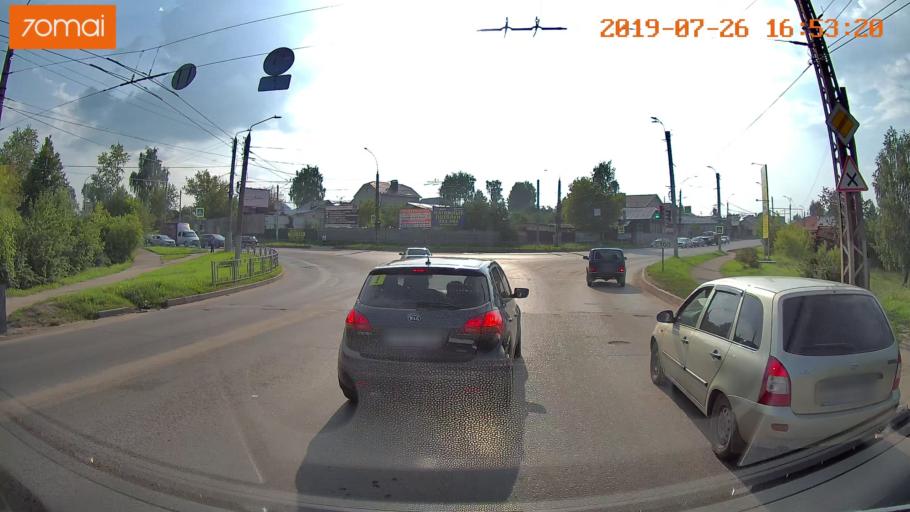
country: RU
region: Ivanovo
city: Bogorodskoye
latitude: 57.0168
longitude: 41.0033
